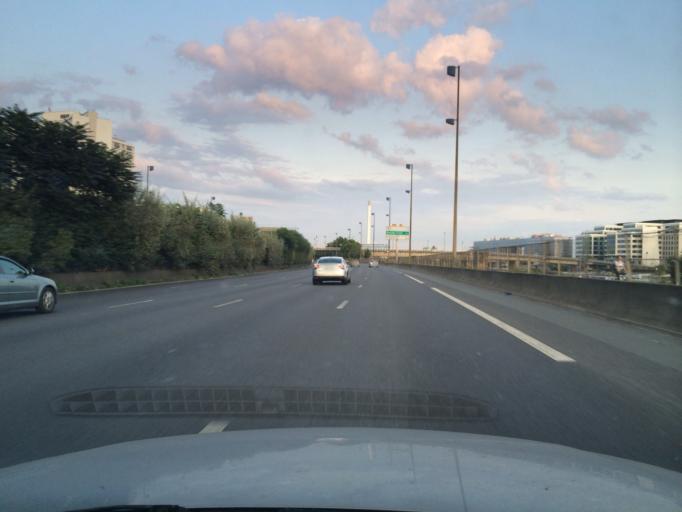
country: FR
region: Ile-de-France
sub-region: Departement du Val-de-Marne
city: Ivry-sur-Seine
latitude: 48.8231
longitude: 2.3954
